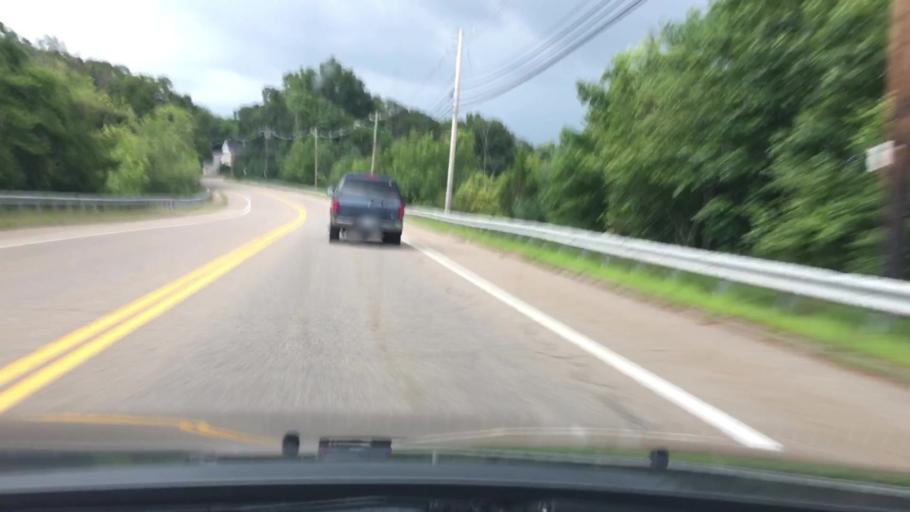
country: US
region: Massachusetts
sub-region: Norfolk County
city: Plainville
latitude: 41.9665
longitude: -71.3454
